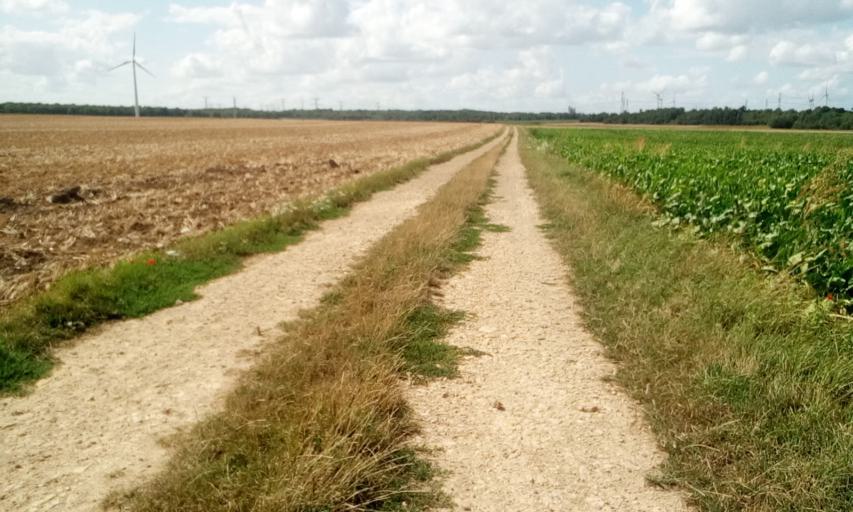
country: FR
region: Lower Normandy
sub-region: Departement du Calvados
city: Bellengreville
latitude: 49.1087
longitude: -0.2255
